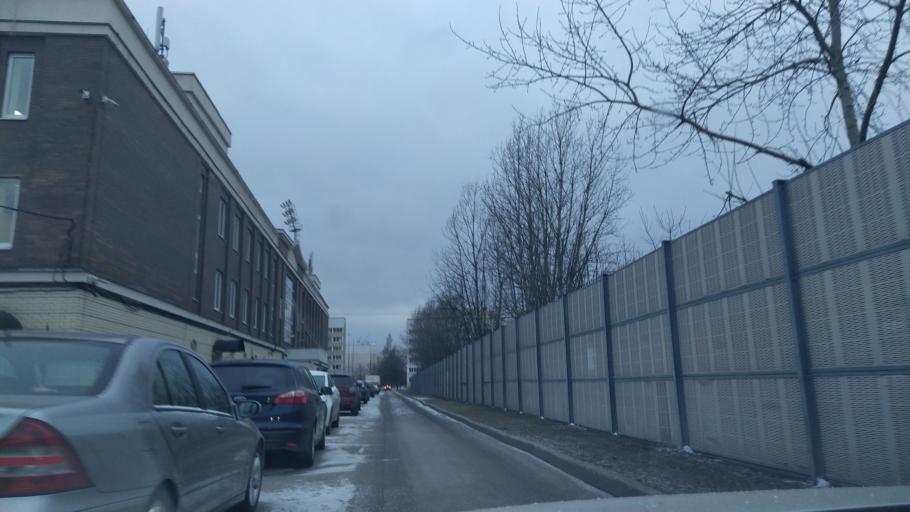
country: RU
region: St.-Petersburg
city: Pushkin
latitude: 59.7326
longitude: 30.4072
